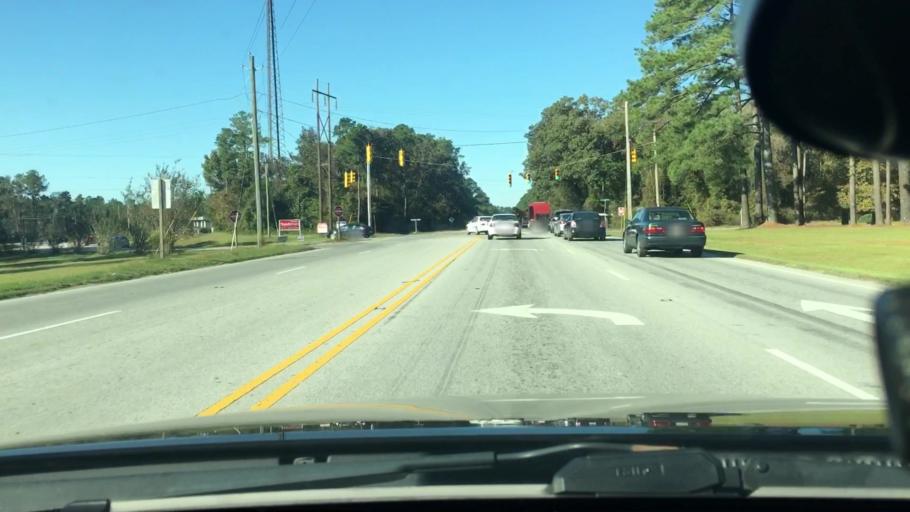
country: US
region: North Carolina
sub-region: Craven County
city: Vanceboro
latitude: 35.2159
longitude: -77.1206
